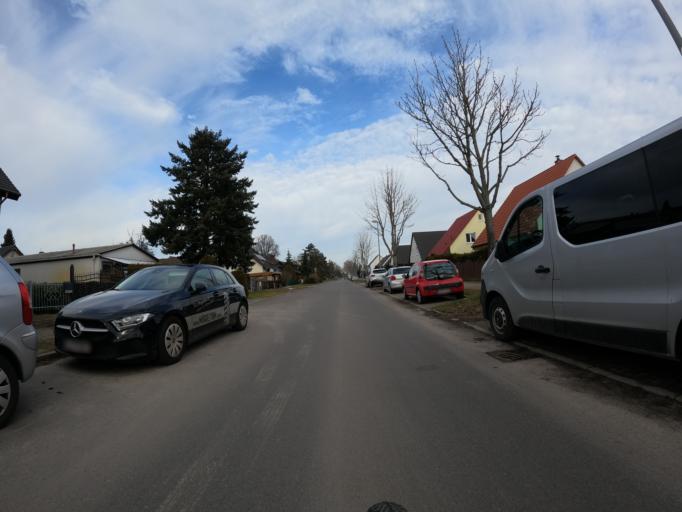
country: DE
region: Berlin
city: Mahlsdorf
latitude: 52.5199
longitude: 13.6354
